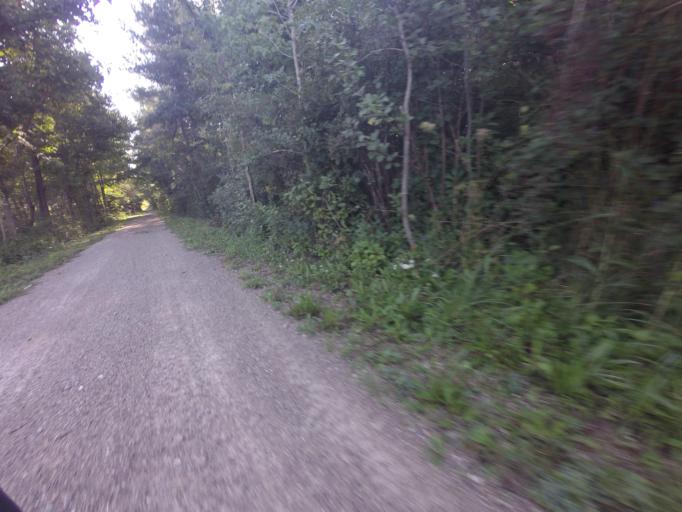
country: CA
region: Ontario
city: Huron East
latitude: 43.7379
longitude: -81.4532
